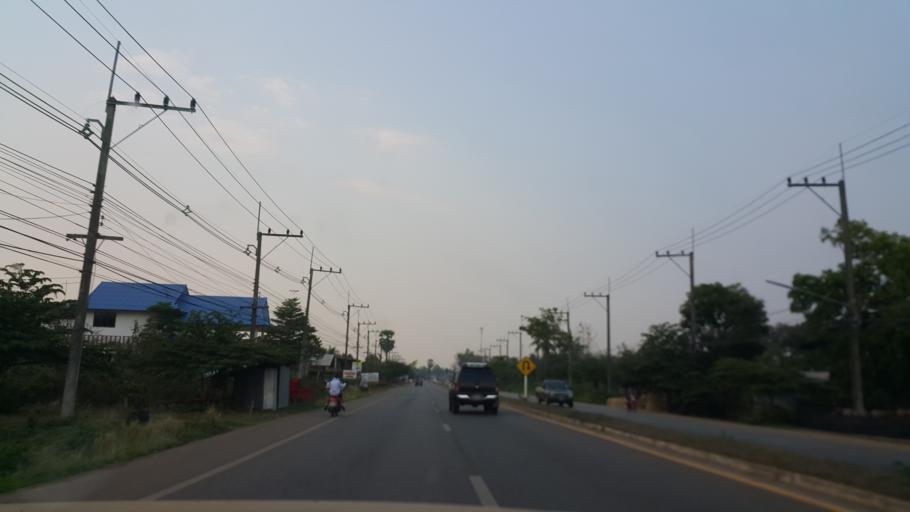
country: TH
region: Nakhon Phanom
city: Renu Nakhon
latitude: 17.0035
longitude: 104.7232
